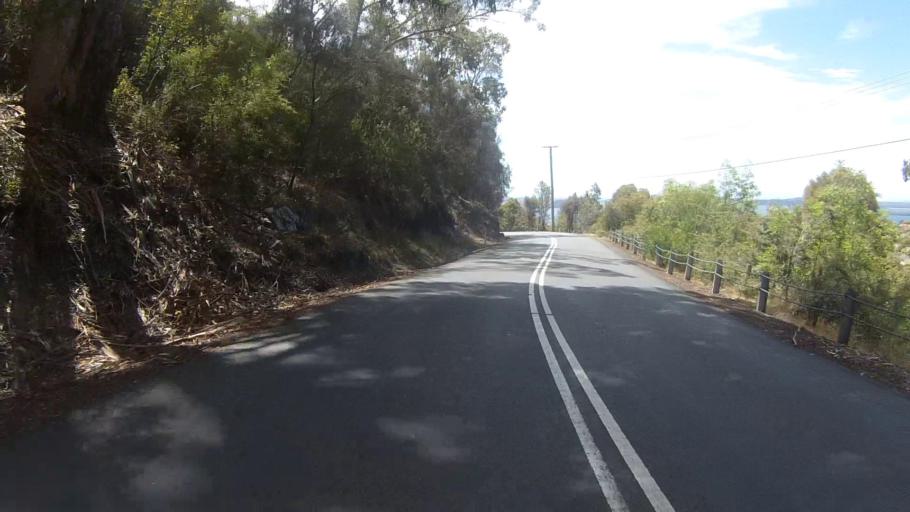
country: AU
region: Tasmania
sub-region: Kingborough
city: Kingston Beach
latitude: -42.9614
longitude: 147.3309
